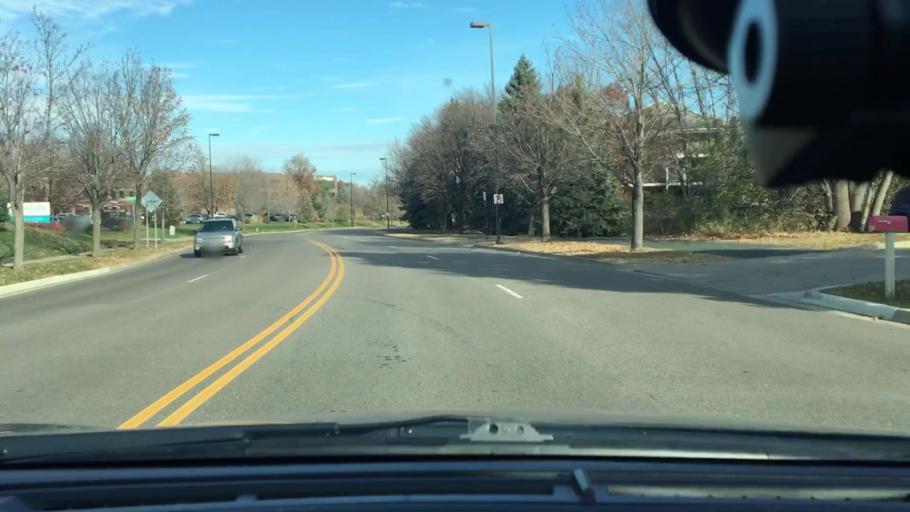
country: US
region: Minnesota
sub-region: Hennepin County
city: Maple Grove
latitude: 45.0679
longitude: -93.4430
